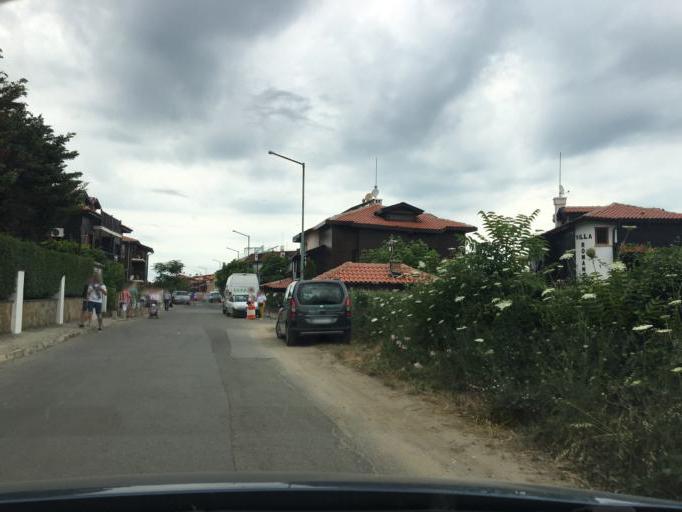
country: BG
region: Burgas
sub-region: Obshtina Sozopol
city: Sozopol
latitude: 42.4065
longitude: 27.7106
